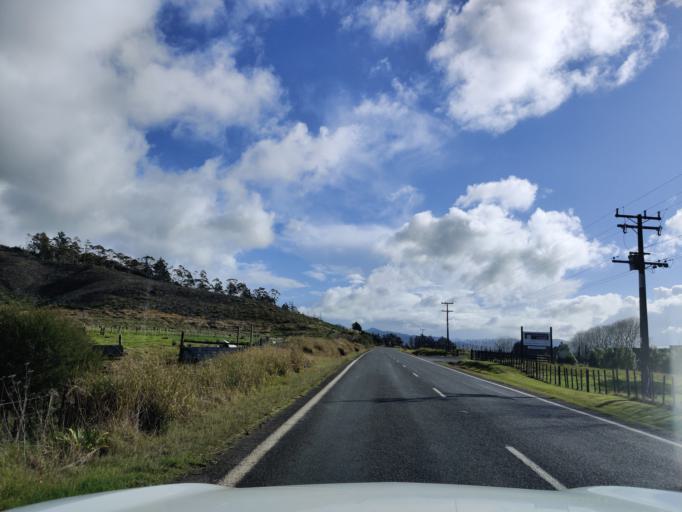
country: NZ
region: Waikato
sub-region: Thames-Coromandel District
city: Whitianga
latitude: -36.7489
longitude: 175.6784
